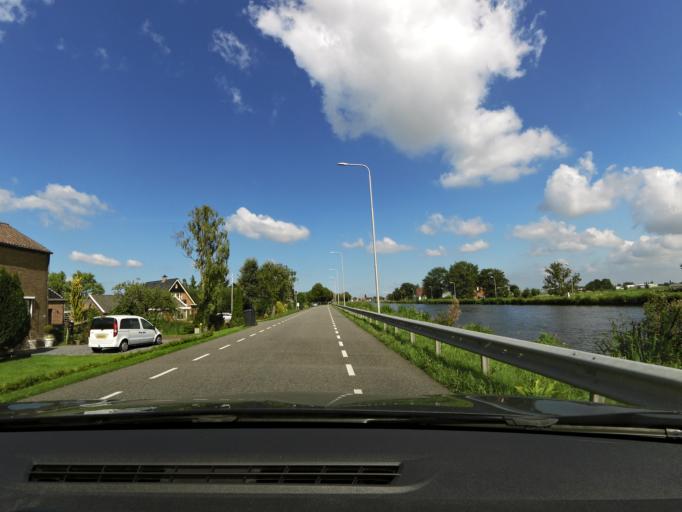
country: NL
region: South Holland
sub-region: Gemeente Nieuwkoop
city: Nieuwkoop
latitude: 52.1726
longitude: 4.7143
